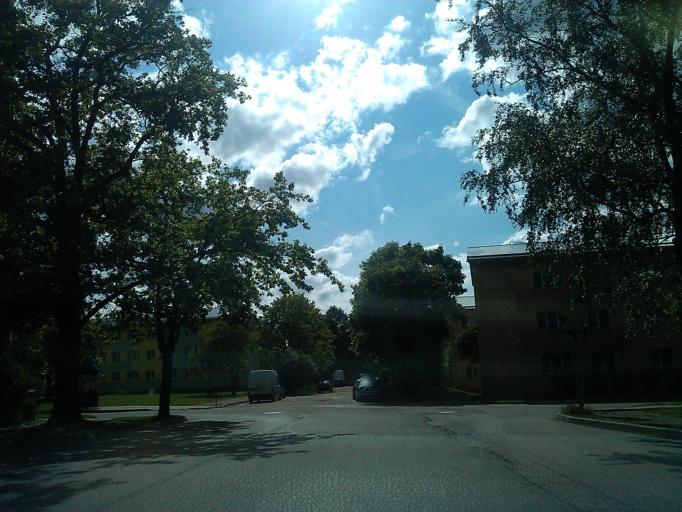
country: LV
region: Cesu Rajons
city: Cesis
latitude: 57.3059
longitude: 25.2792
